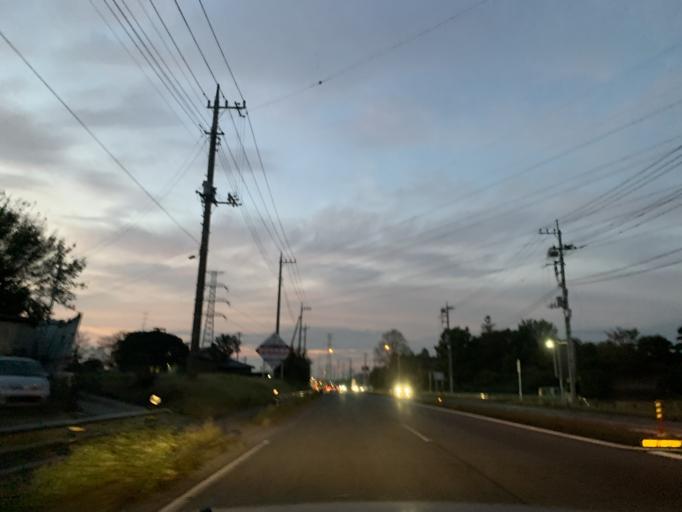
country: JP
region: Chiba
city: Nagareyama
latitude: 35.9200
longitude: 139.9239
